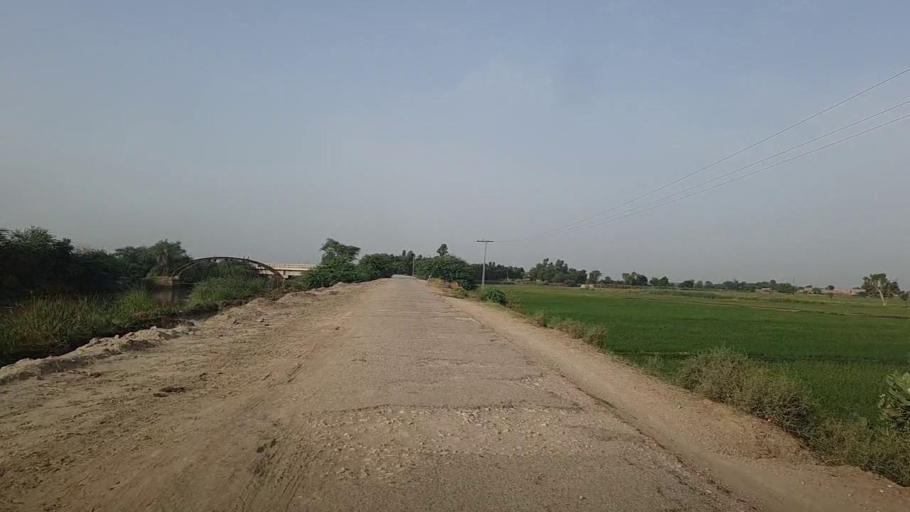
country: PK
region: Sindh
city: Mehar
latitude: 27.1296
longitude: 67.7899
